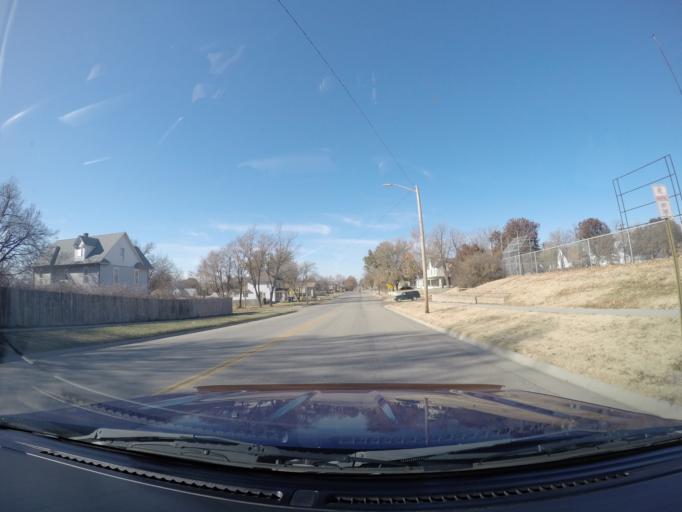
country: US
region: Kansas
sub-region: Clay County
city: Clay Center
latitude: 39.3803
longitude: -97.1217
